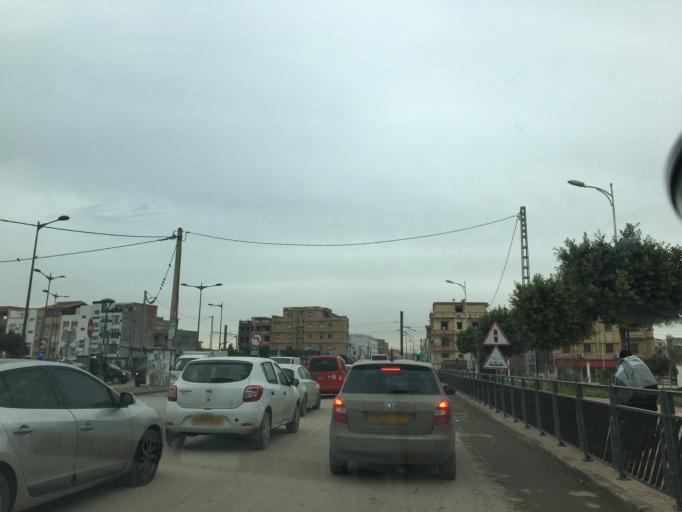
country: DZ
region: Alger
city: Ain Taya
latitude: 36.7769
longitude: 3.2511
